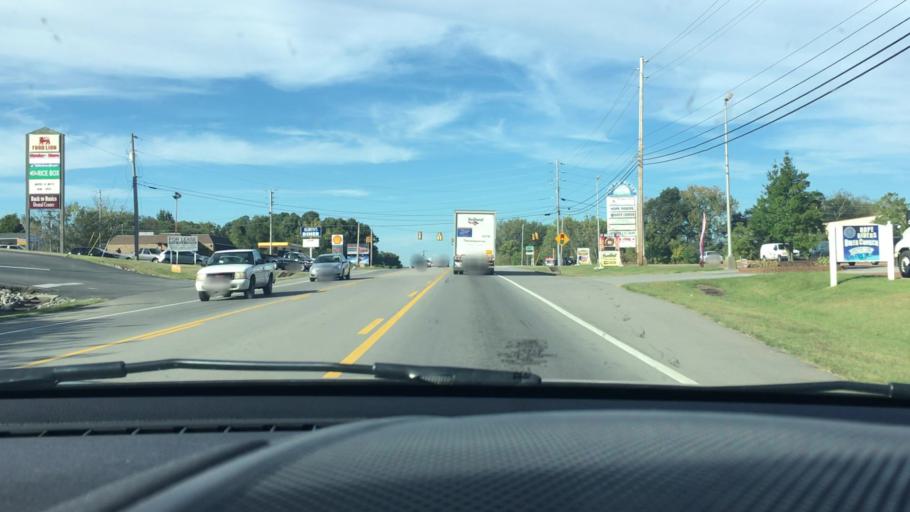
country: US
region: Tennessee
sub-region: Montgomery County
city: Clarksville
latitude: 36.4775
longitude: -87.3759
